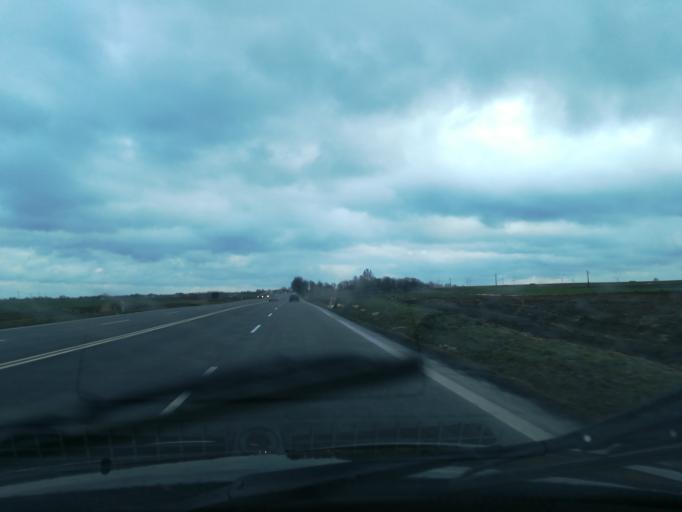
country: PL
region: Subcarpathian Voivodeship
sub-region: Powiat lancucki
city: Kosina
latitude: 50.0761
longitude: 22.3020
